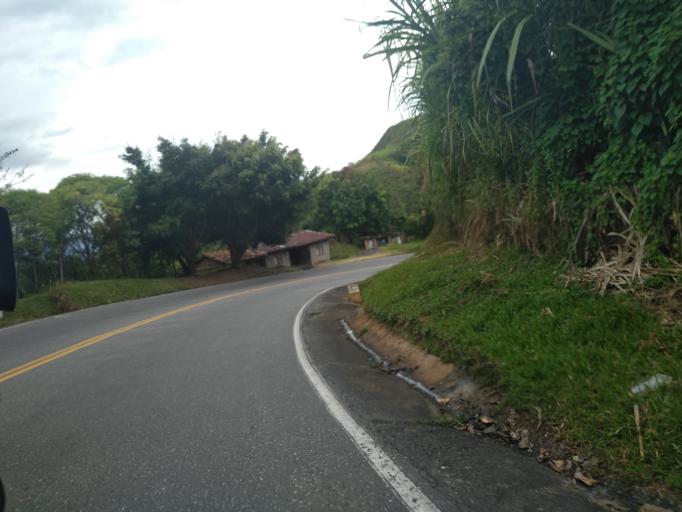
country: CO
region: Cauca
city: Rosas
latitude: 2.2431
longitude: -76.7680
